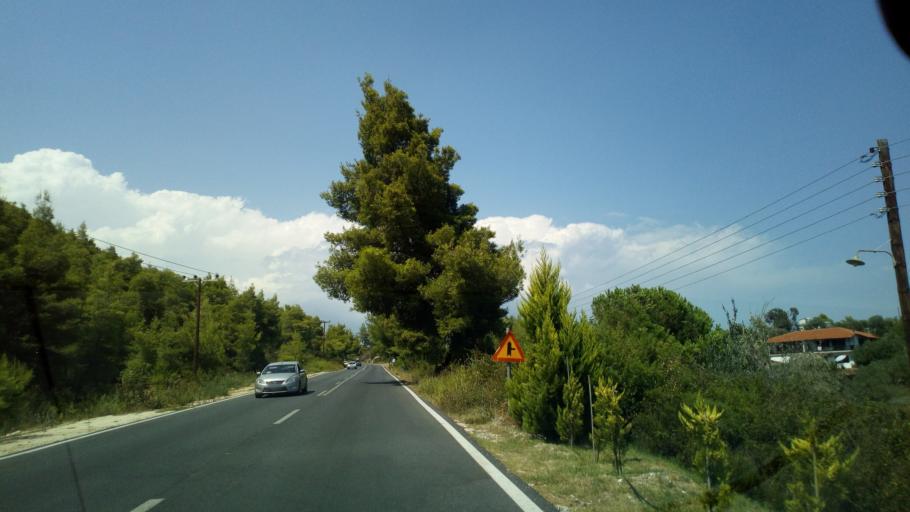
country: GR
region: Central Macedonia
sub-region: Nomos Chalkidikis
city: Agios Nikolaos
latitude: 40.2065
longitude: 23.7608
